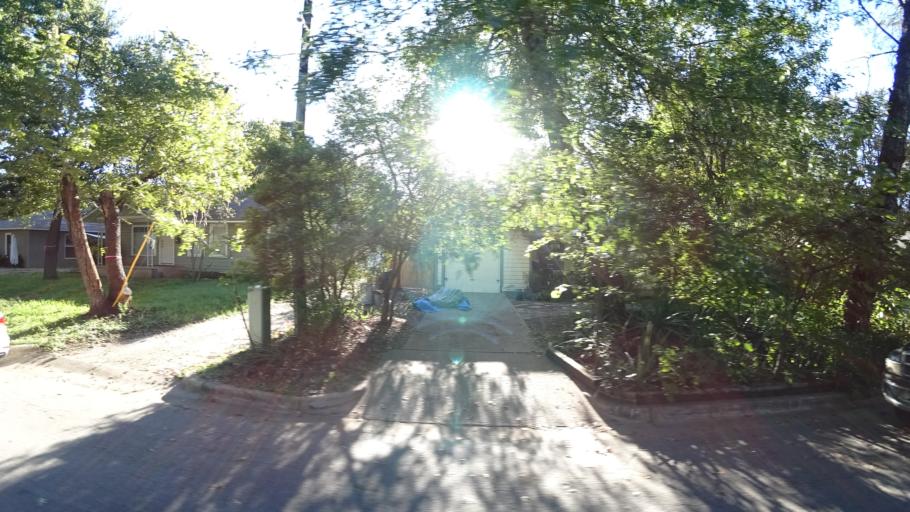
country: US
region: Texas
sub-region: Travis County
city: Austin
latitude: 30.3095
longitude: -97.7197
